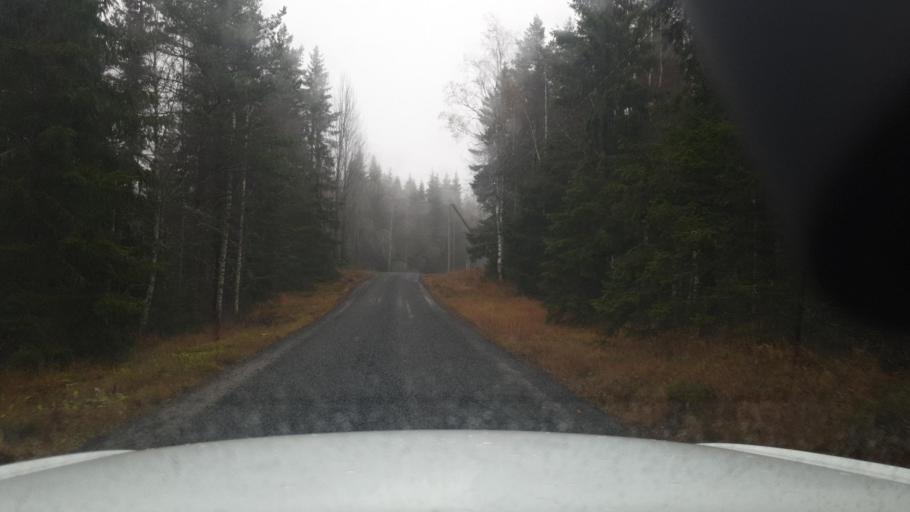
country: SE
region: Vaermland
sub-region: Eda Kommun
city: Charlottenberg
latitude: 60.1597
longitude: 12.6020
